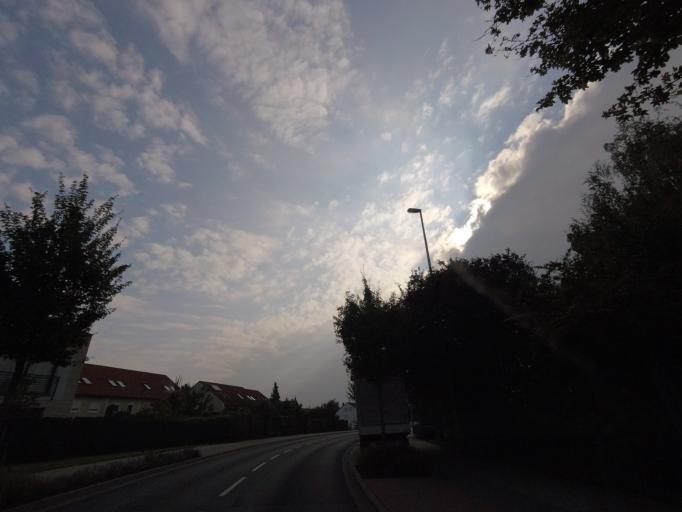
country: DE
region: Hesse
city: Liederbach
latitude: 50.1212
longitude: 8.4823
